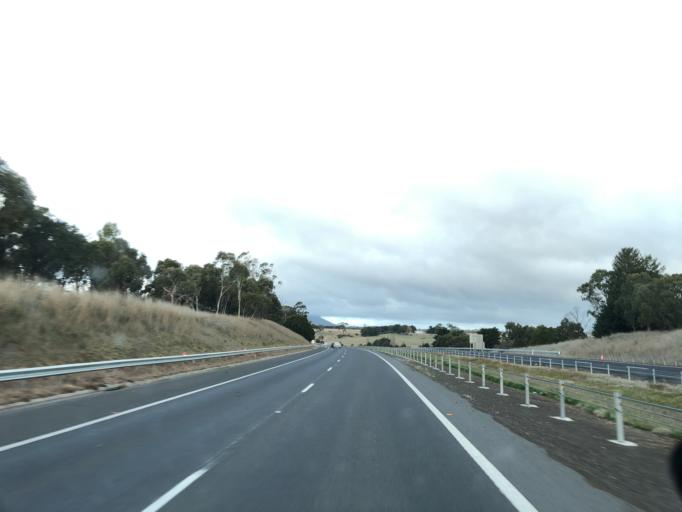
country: AU
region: Victoria
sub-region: Mount Alexander
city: Castlemaine
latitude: -37.2655
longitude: 144.4740
